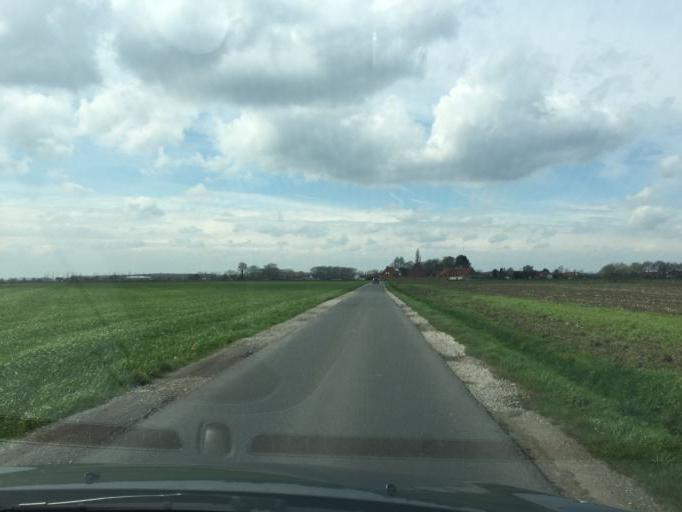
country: BE
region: Flanders
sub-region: Provincie Oost-Vlaanderen
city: Aalter
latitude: 51.0672
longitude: 3.4493
